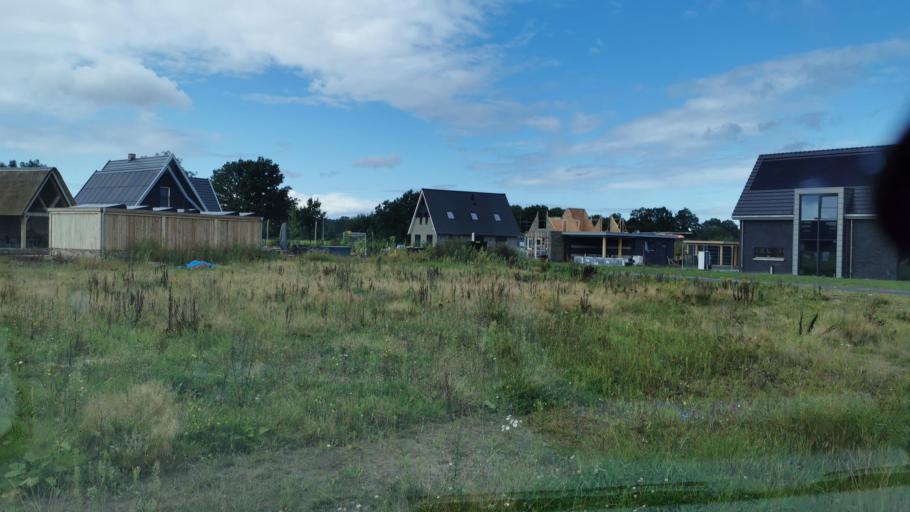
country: NL
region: Overijssel
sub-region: Gemeente Losser
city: Losser
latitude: 52.2696
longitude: 6.9988
